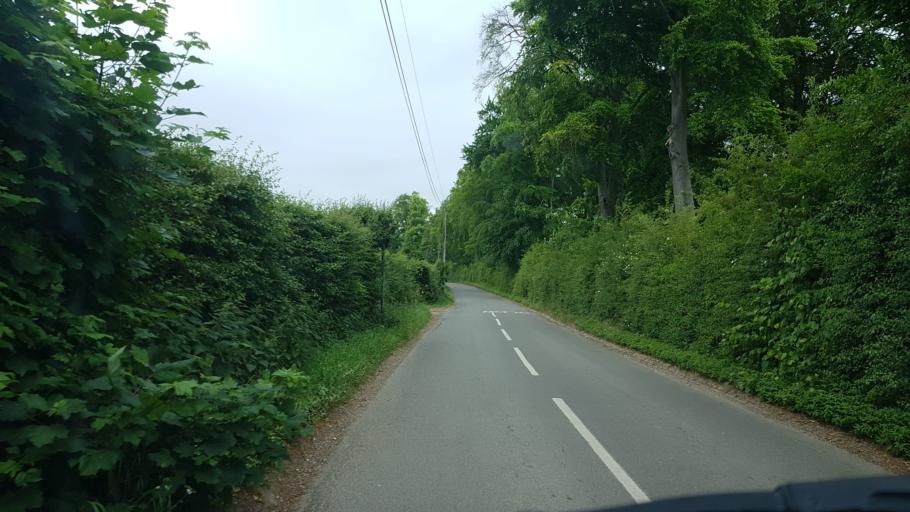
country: GB
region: England
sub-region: Surrey
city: Great Bookham
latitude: 51.2673
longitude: -0.3663
